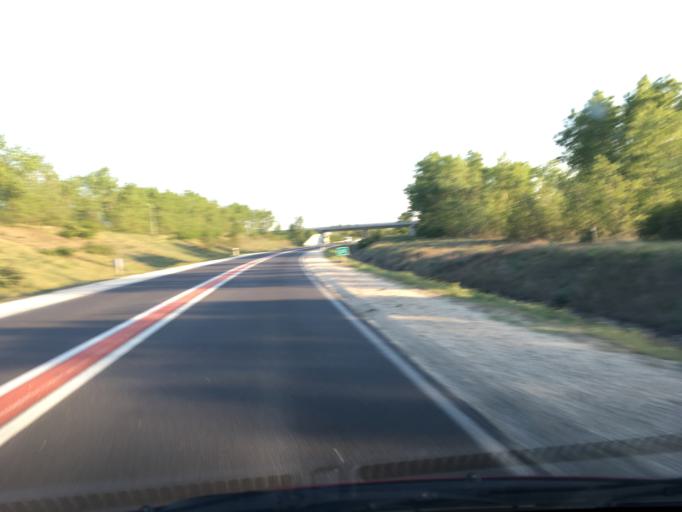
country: HU
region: Pest
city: Fot
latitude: 47.6370
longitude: 19.1694
